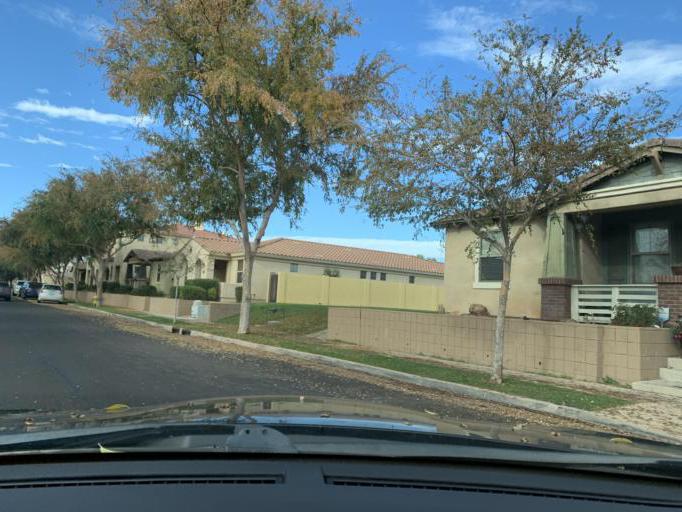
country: US
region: Arizona
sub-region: Maricopa County
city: Gilbert
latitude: 33.3257
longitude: -111.7165
